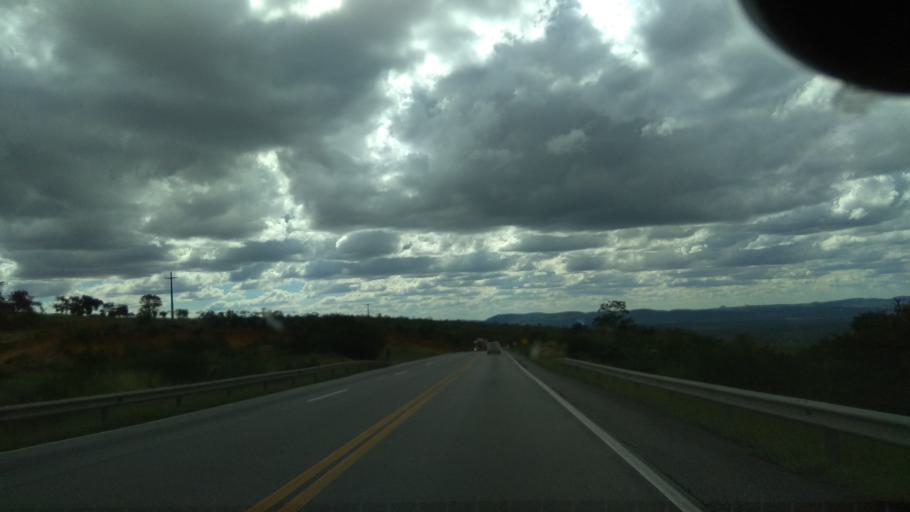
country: BR
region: Bahia
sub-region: Santa Ines
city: Santa Ines
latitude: -13.0565
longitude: -39.9582
